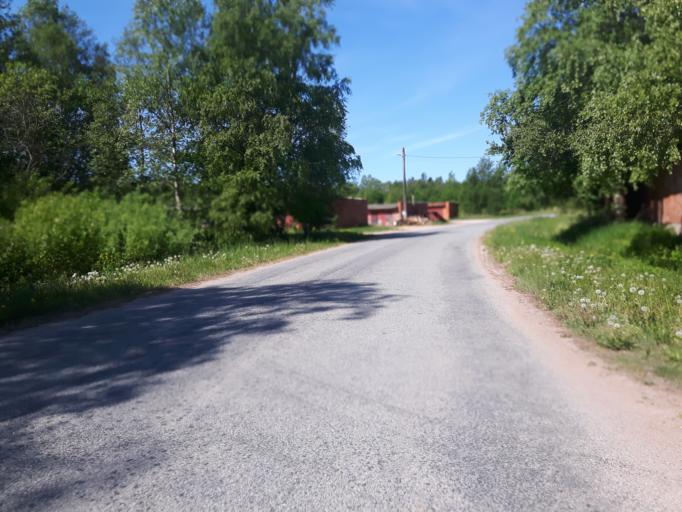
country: EE
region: Ida-Virumaa
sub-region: Aseri vald
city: Aseri
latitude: 59.4506
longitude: 26.8575
